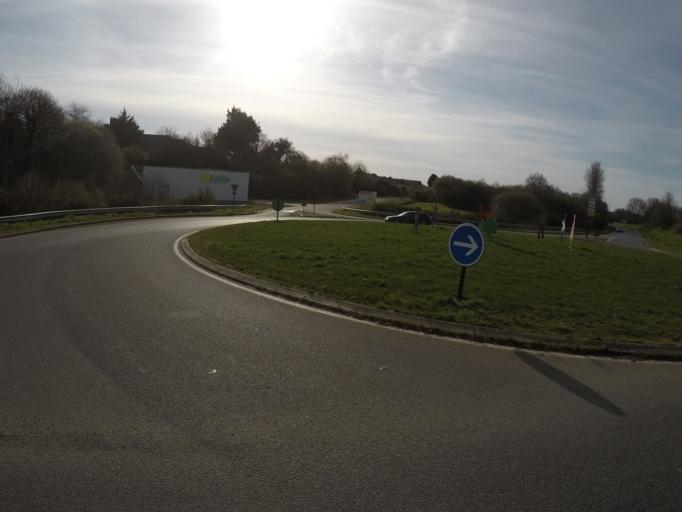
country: FR
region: Brittany
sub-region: Departement des Cotes-d'Armor
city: Plouagat
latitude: 48.5293
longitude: -2.9682
